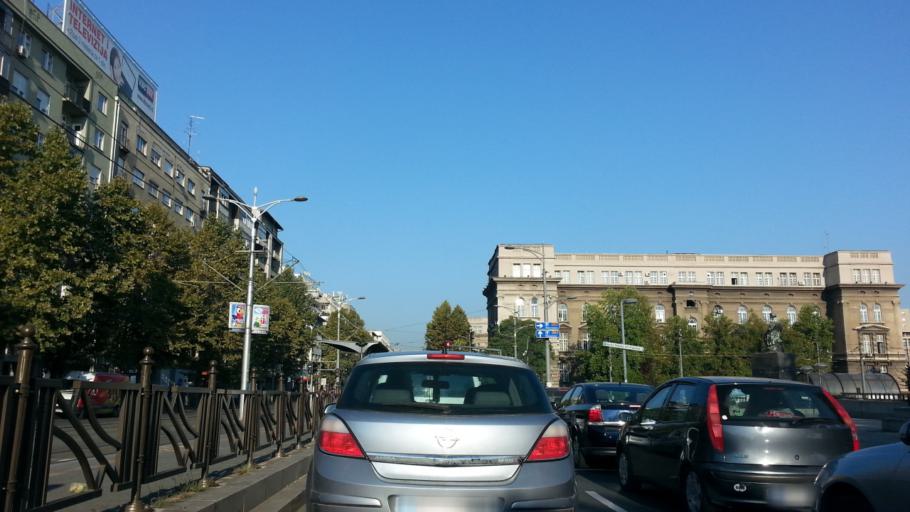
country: RS
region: Central Serbia
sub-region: Belgrade
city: Vracar
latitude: 44.8044
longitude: 20.4781
